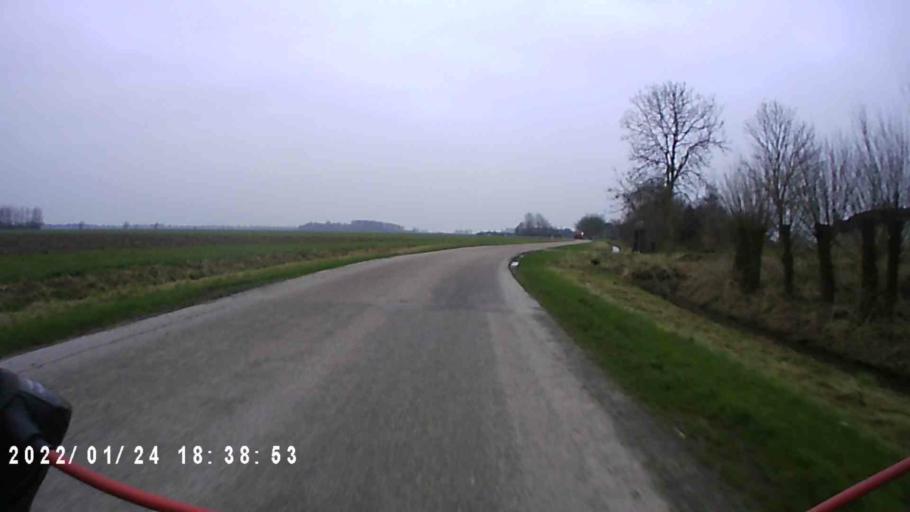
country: NL
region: Groningen
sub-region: Gemeente De Marne
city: Ulrum
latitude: 53.3476
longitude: 6.3373
